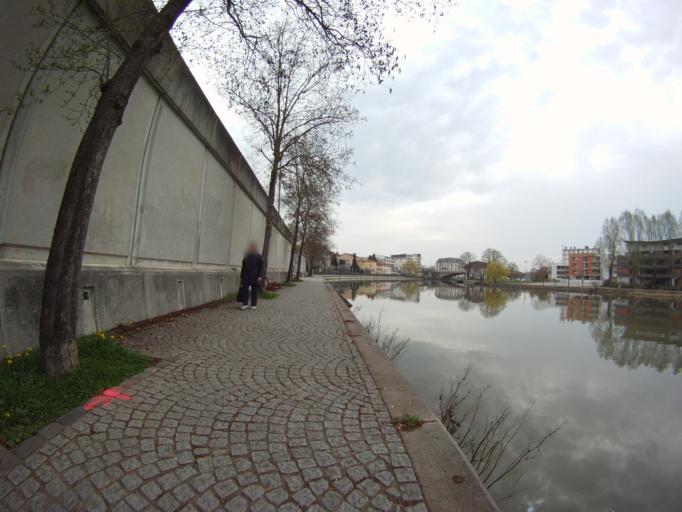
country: FR
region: Lorraine
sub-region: Departement de Meurthe-et-Moselle
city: Saint-Max
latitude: 48.7004
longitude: 6.2000
